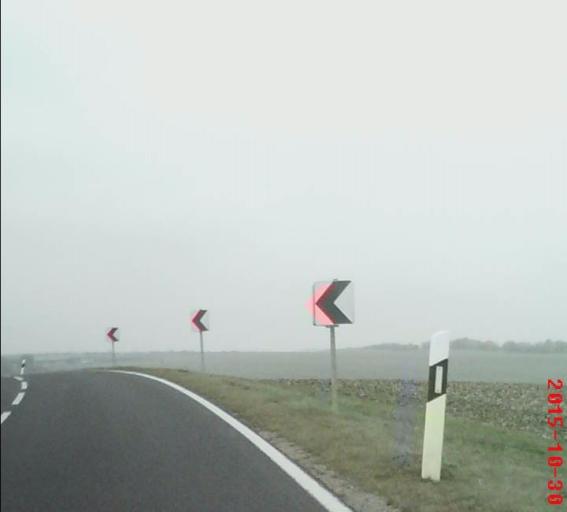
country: DE
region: Thuringia
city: Kullstedt
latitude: 51.2832
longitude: 10.2671
